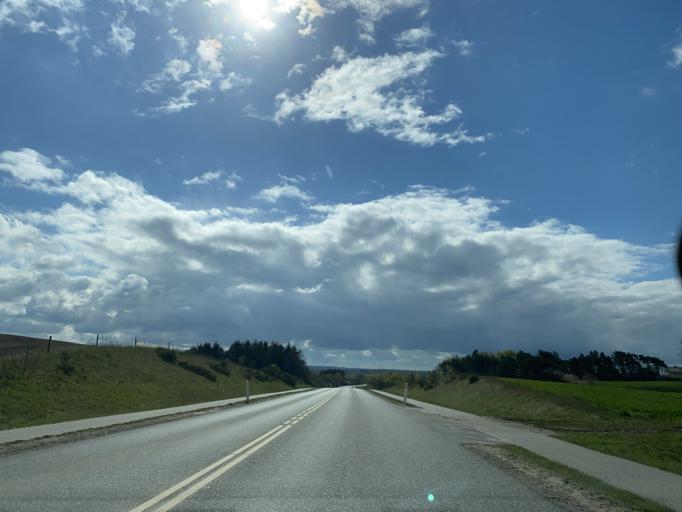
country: DK
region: Central Jutland
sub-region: Viborg Kommune
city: Bjerringbro
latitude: 56.2877
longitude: 9.6051
